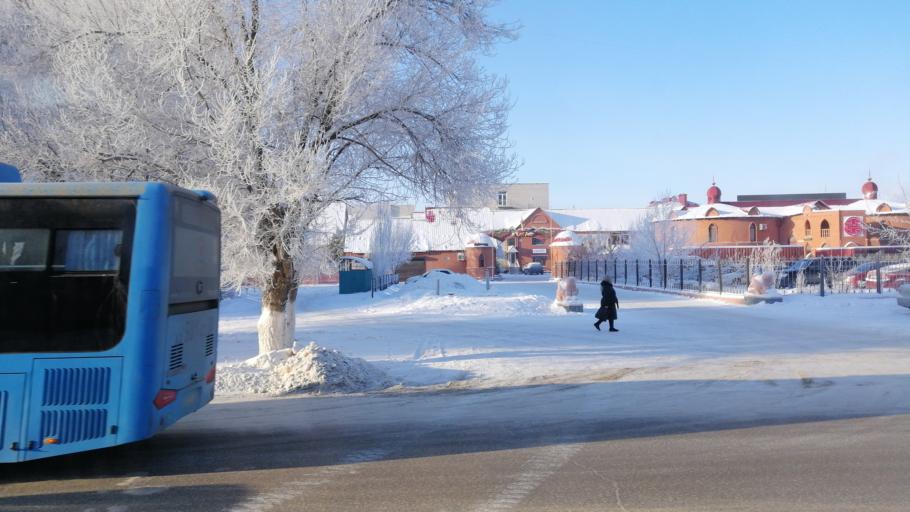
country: KZ
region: Aqtoebe
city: Aqtobe
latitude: 50.2938
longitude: 57.1484
